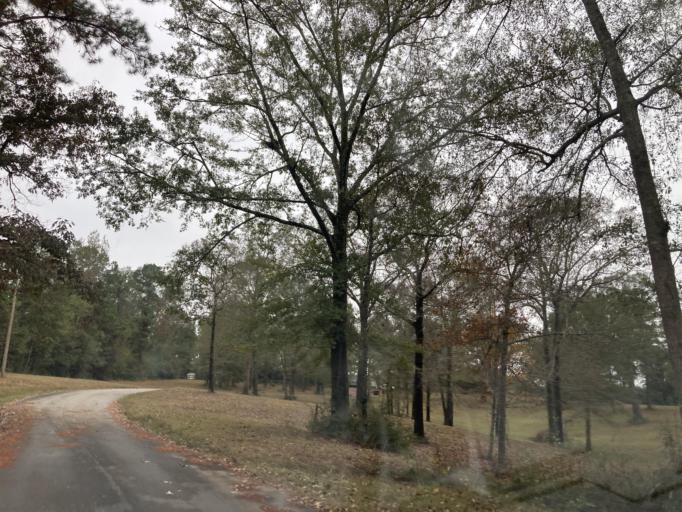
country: US
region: Mississippi
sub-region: Lamar County
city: Purvis
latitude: 31.1862
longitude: -89.4117
